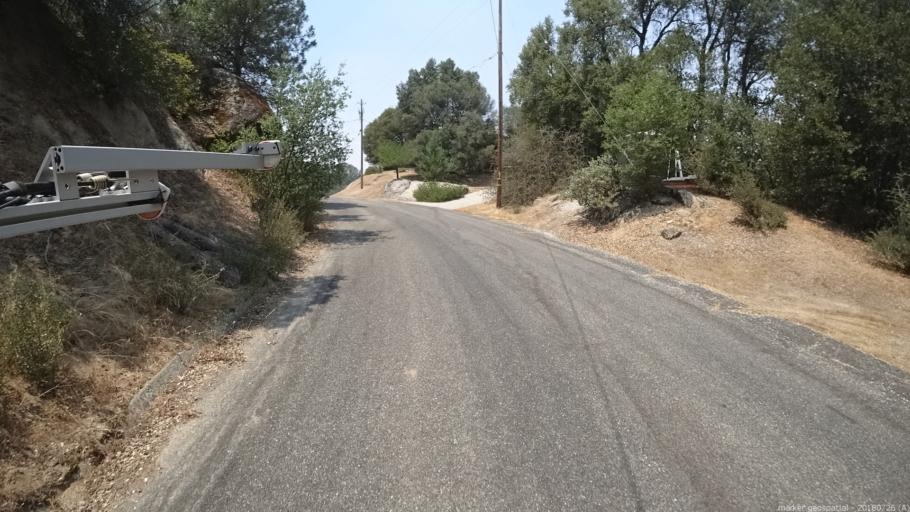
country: US
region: California
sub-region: Madera County
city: Oakhurst
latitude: 37.3096
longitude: -119.6396
